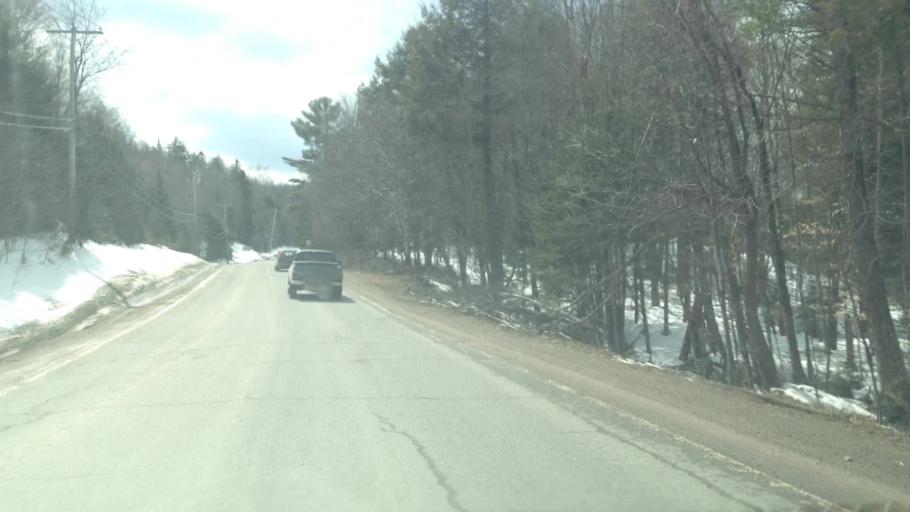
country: CA
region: Quebec
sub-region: Laurentides
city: Brownsburg-Chatham
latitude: 45.7292
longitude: -74.4761
